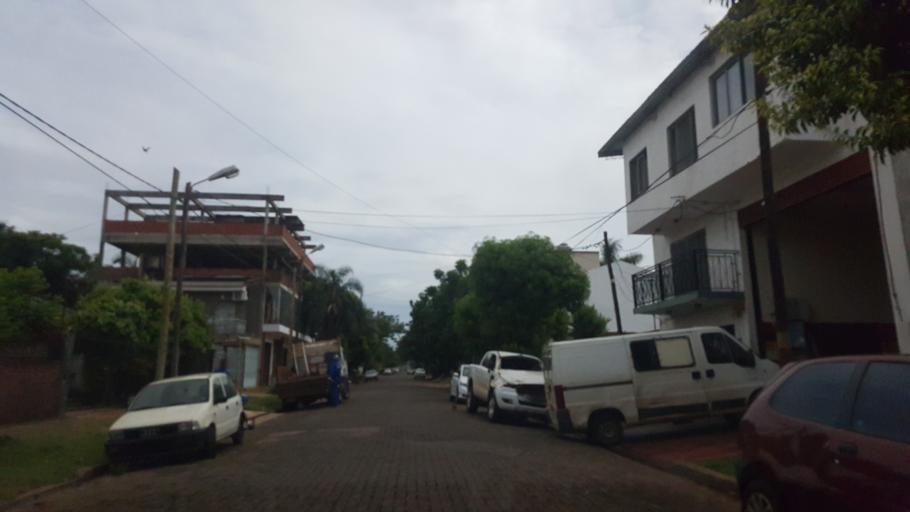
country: AR
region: Misiones
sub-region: Departamento de Capital
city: Posadas
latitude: -27.3878
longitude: -55.9018
